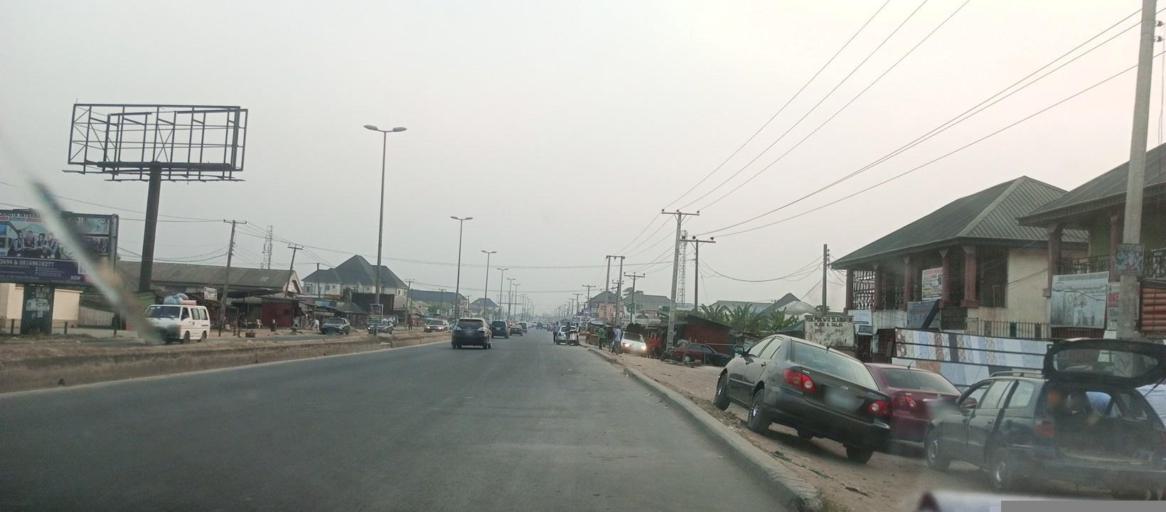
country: NG
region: Rivers
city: Emuoha
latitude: 4.9181
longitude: 6.9971
